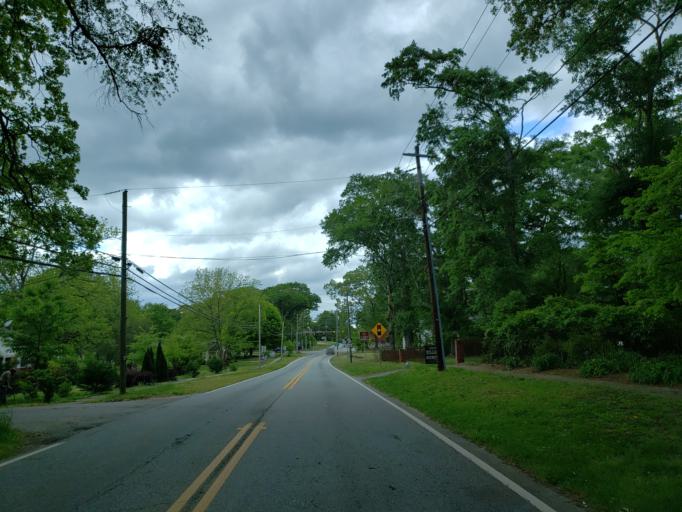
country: US
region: Georgia
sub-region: Haralson County
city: Tallapoosa
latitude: 33.7527
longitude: -85.2923
